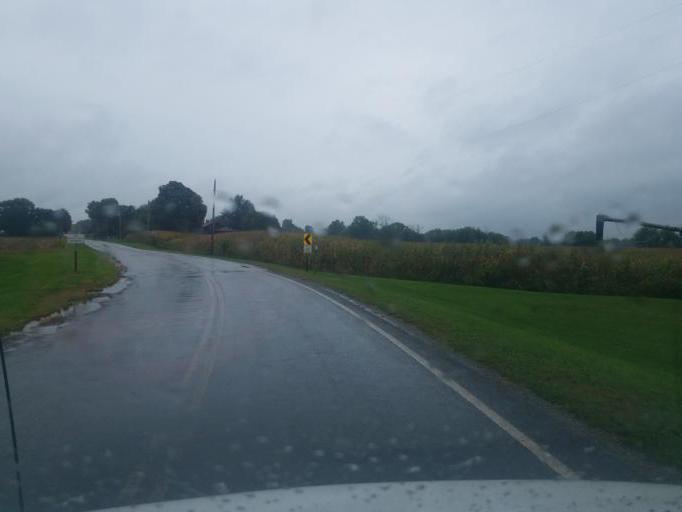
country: US
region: Ohio
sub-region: Medina County
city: Seville
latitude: 40.9891
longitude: -81.8589
